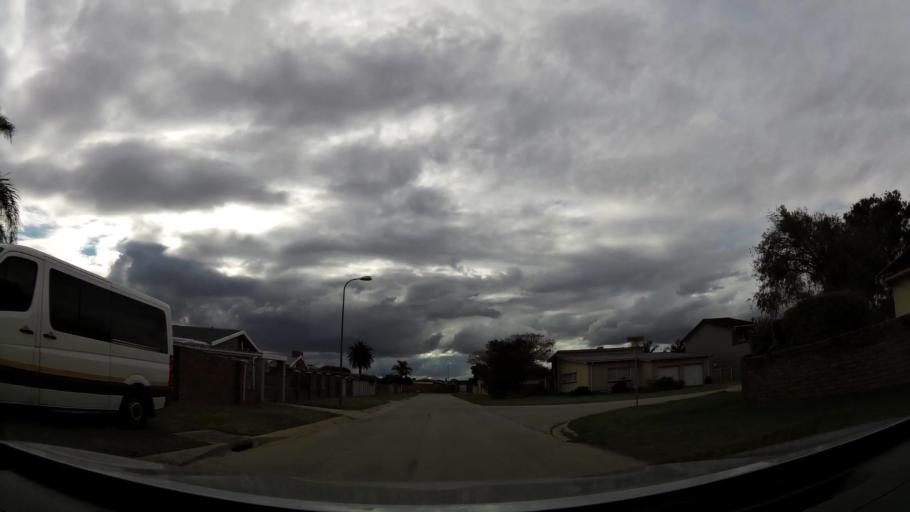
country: ZA
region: Eastern Cape
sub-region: Nelson Mandela Bay Metropolitan Municipality
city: Port Elizabeth
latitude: -33.9393
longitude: 25.4742
